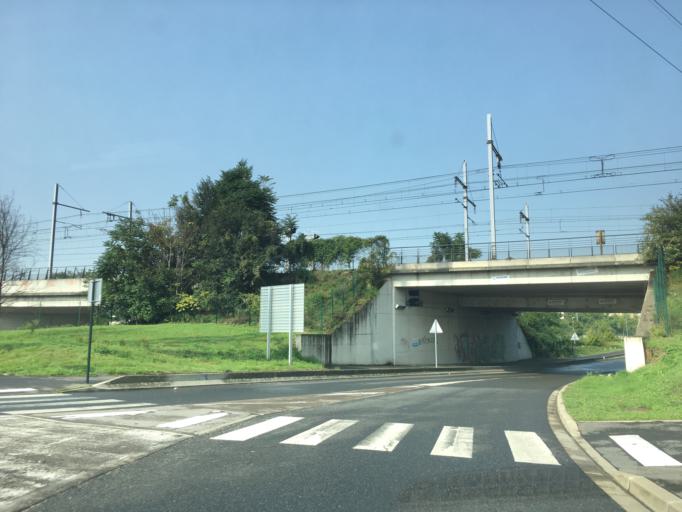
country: FR
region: Ile-de-France
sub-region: Departement du Val-de-Marne
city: Boissy-Saint-Leger
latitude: 48.7560
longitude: 2.5074
